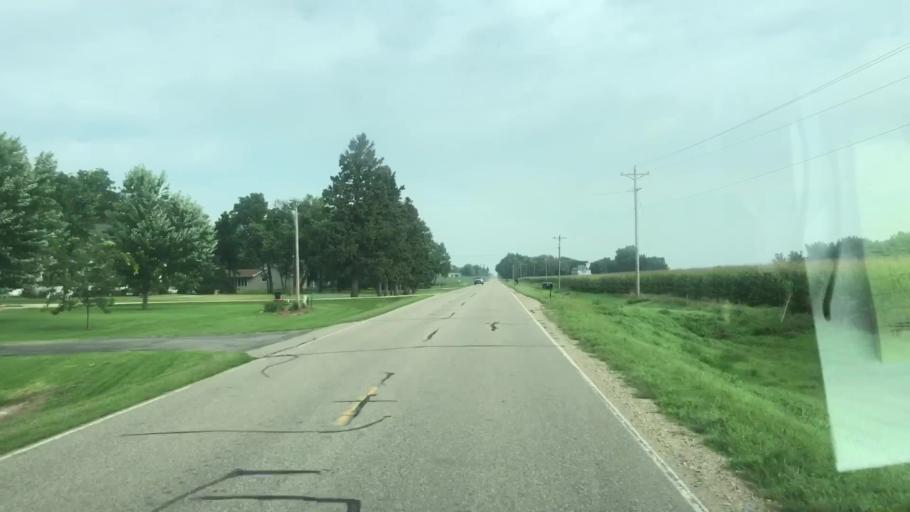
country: US
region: Iowa
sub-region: O'Brien County
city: Sheldon
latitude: 43.1954
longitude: -95.8622
